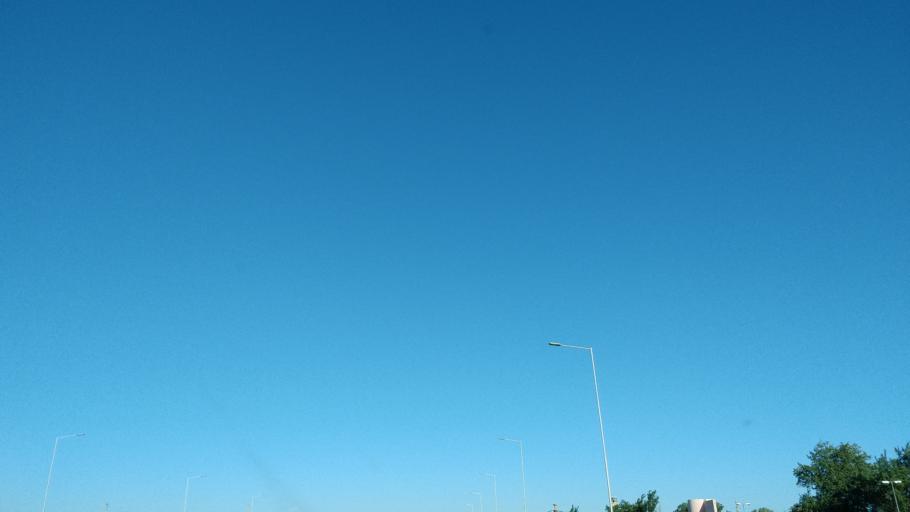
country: AR
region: Cordoba
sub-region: Departamento de Capital
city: Cordoba
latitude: -31.3609
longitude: -64.1568
